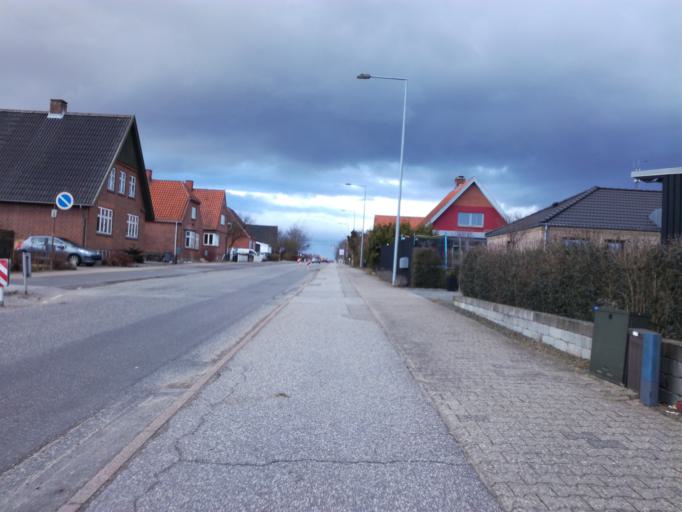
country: DK
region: South Denmark
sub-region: Fredericia Kommune
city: Fredericia
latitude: 55.5795
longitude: 9.7670
